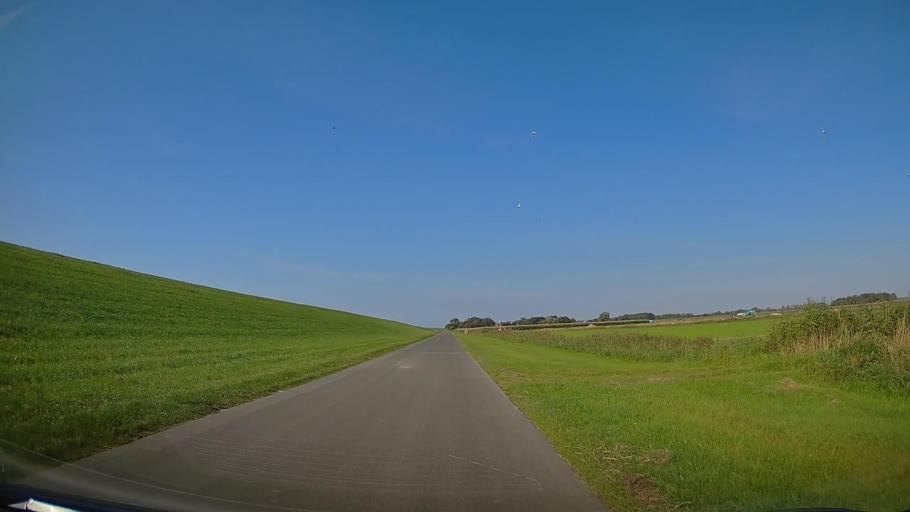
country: DE
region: Lower Saxony
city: Misselwarden
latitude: 53.6643
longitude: 8.4883
